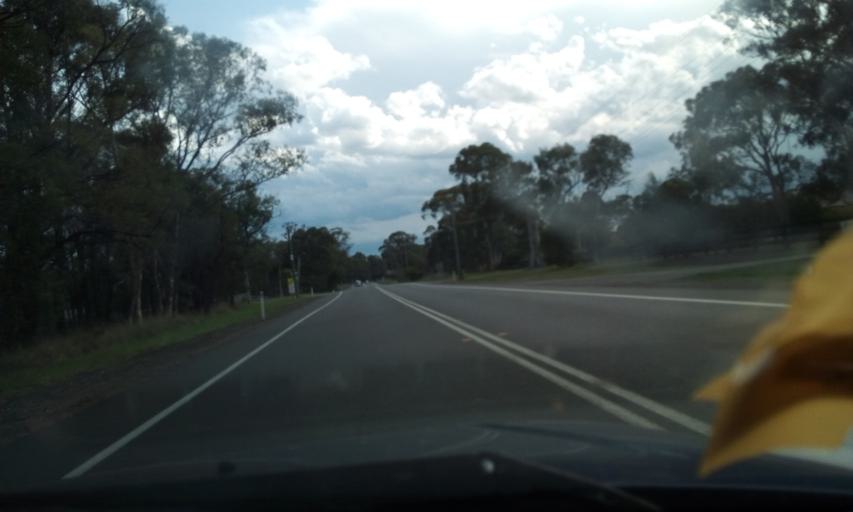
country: AU
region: New South Wales
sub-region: Penrith Municipality
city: Werrington Downs
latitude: -33.6860
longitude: 150.7342
